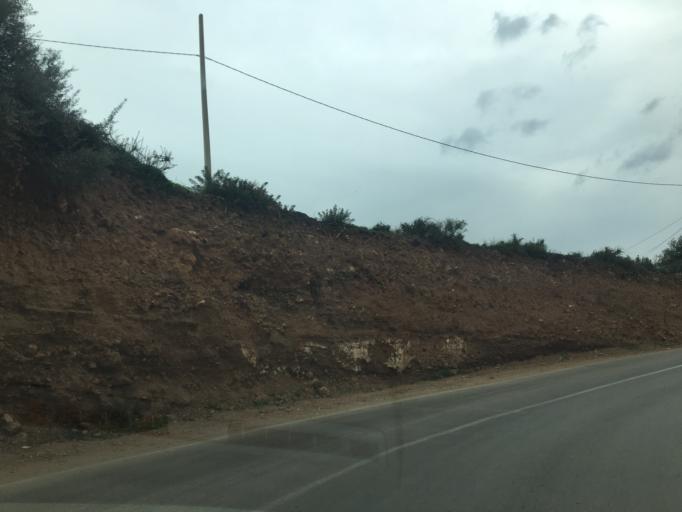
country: DZ
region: Tipaza
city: Tipasa
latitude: 36.6256
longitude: 2.4038
